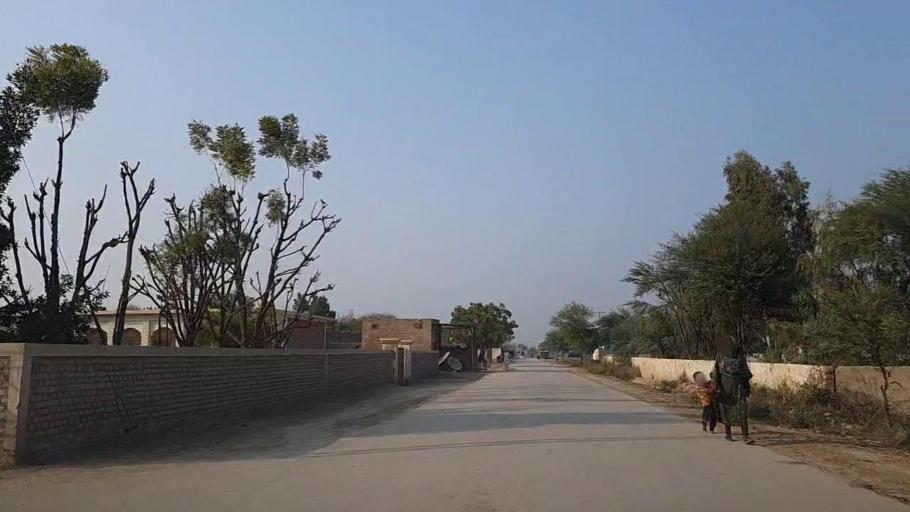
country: PK
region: Sindh
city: Sann
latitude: 26.1244
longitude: 68.1463
